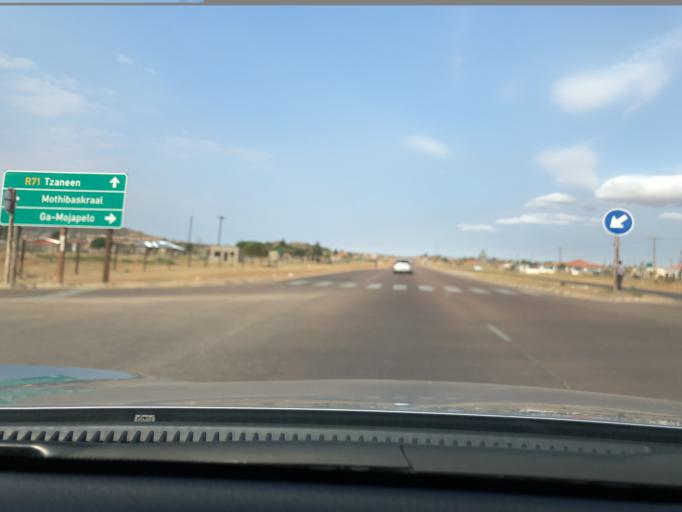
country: ZA
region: Limpopo
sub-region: Capricorn District Municipality
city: Mankoeng
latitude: -23.8925
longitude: 29.6498
